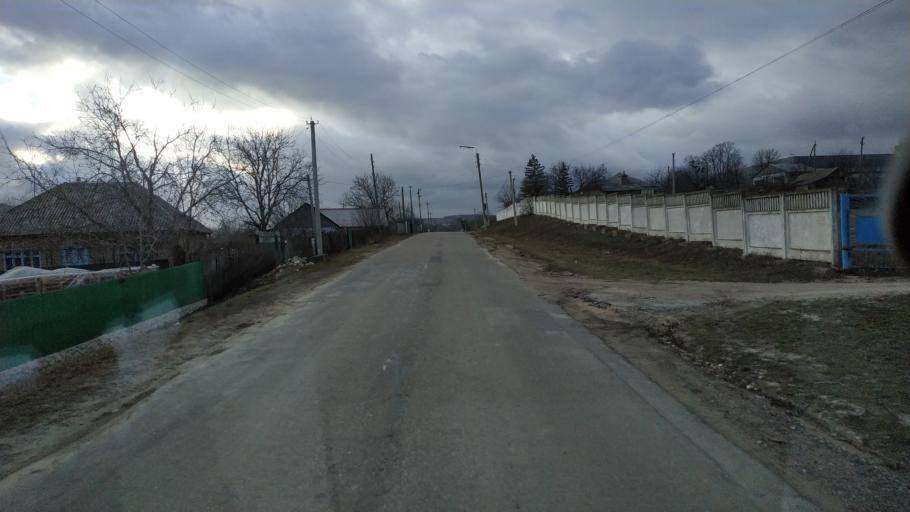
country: MD
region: Calarasi
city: Calarasi
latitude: 47.3069
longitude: 28.3661
